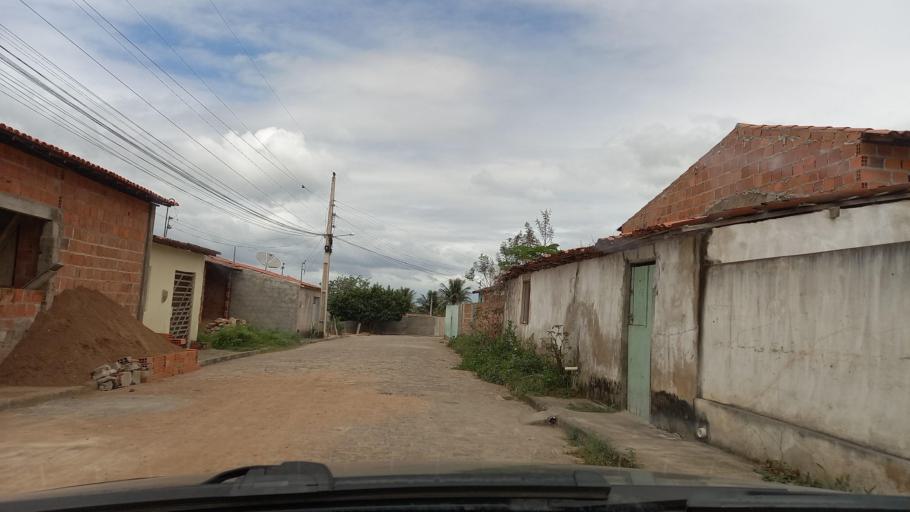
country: BR
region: Sergipe
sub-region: Caninde De Sao Francisco
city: Caninde de Sao Francisco
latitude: -9.6092
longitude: -37.7560
